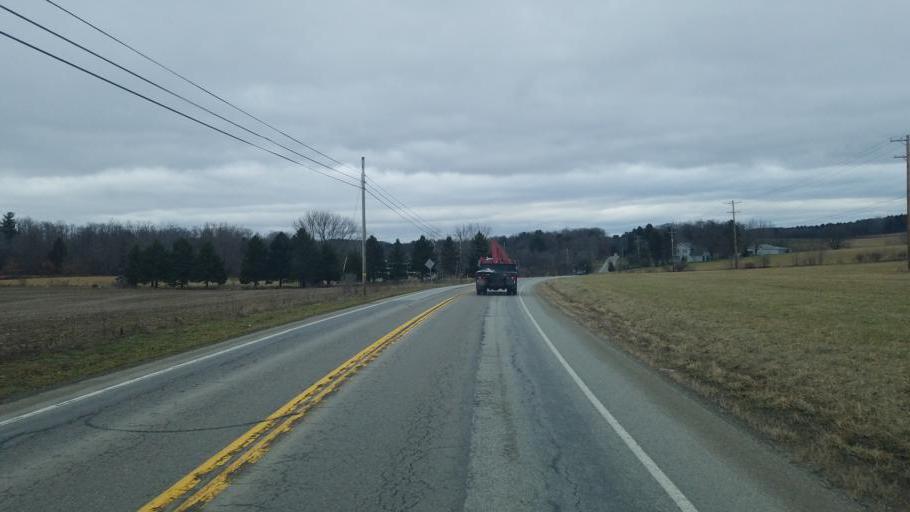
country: US
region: Pennsylvania
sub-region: Clarion County
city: Marianne
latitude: 41.3405
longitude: -79.3499
